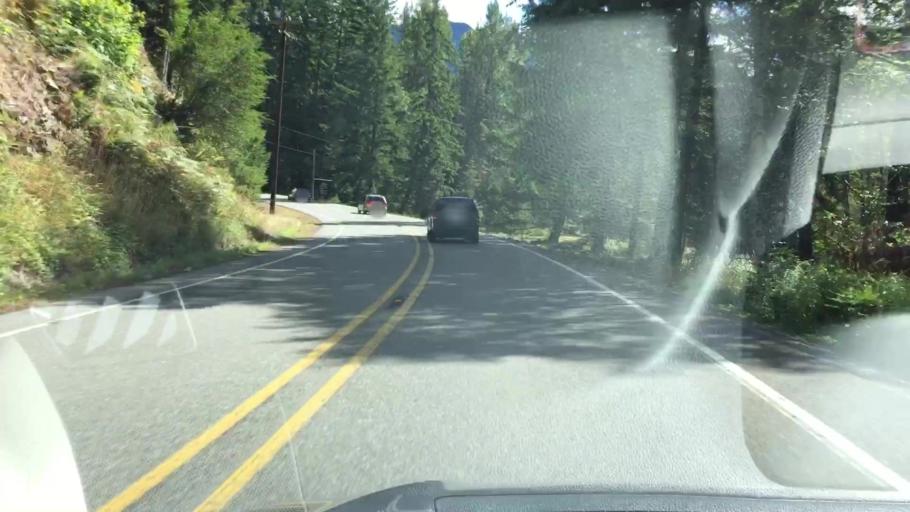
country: US
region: Washington
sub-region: Pierce County
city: Eatonville
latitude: 46.7442
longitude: -121.9235
